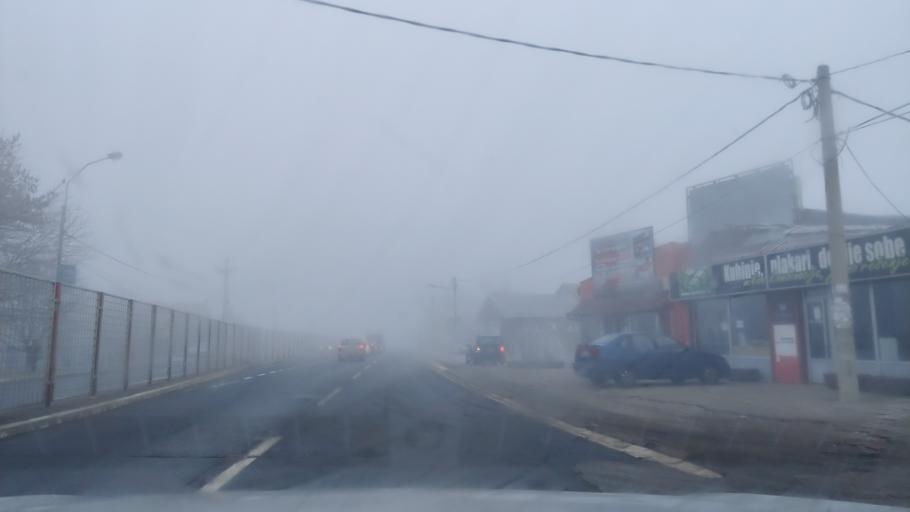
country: RS
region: Central Serbia
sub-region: Belgrade
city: Stari Grad
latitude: 44.8776
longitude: 20.4675
